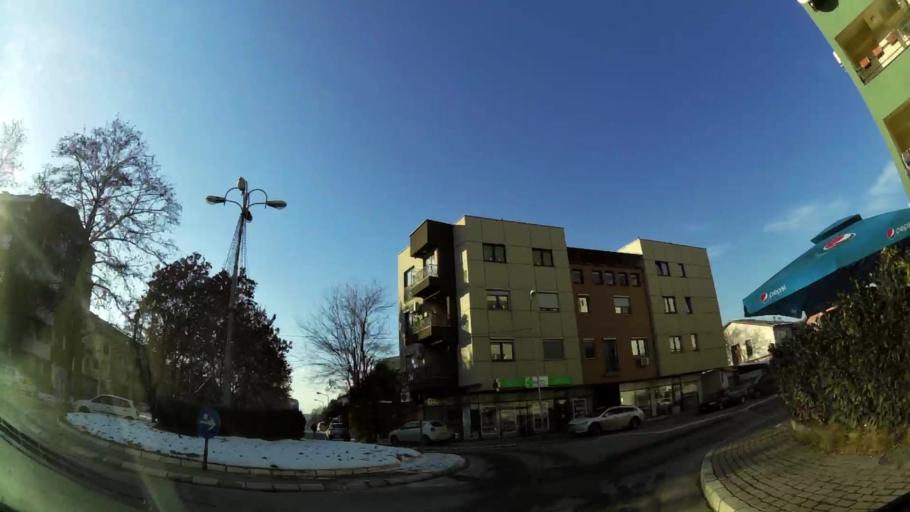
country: MK
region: Karpos
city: Skopje
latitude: 42.0004
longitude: 21.4010
